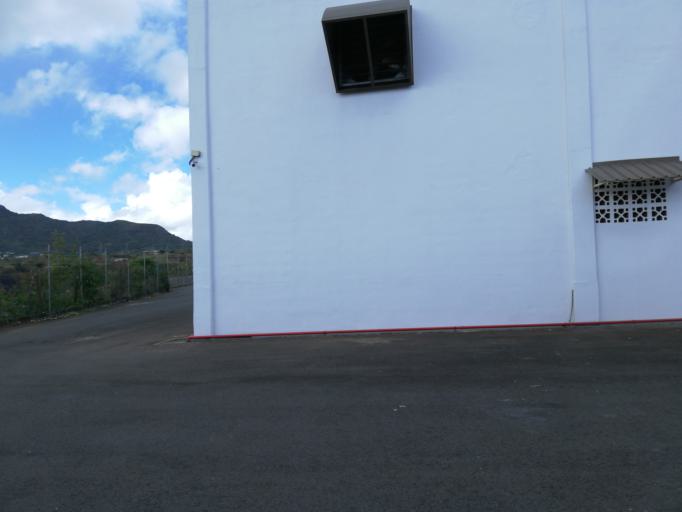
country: MU
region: Moka
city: Pailles
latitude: -20.1913
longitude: 57.4702
